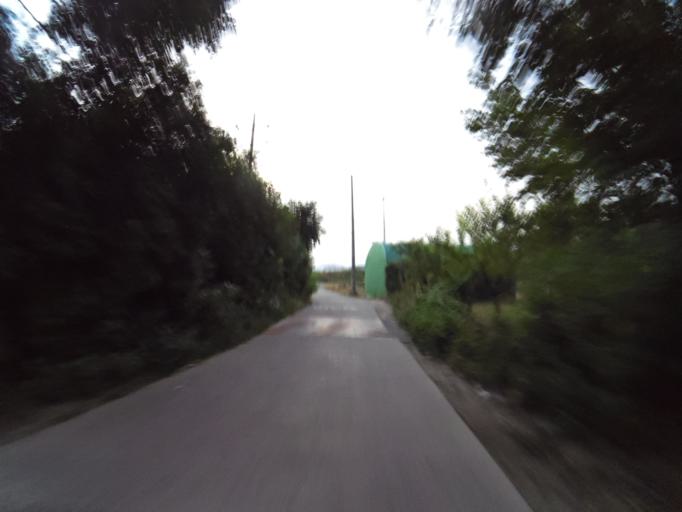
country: KR
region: Gyeongsangbuk-do
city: Gyeongsan-si
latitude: 35.8553
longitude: 128.7408
